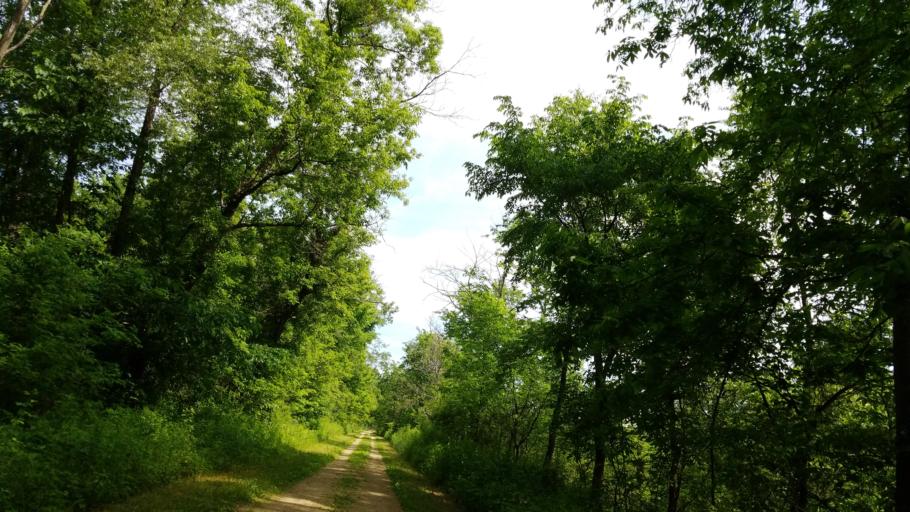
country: US
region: Wisconsin
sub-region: Dunn County
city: Menomonie
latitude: 44.7983
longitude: -91.9472
